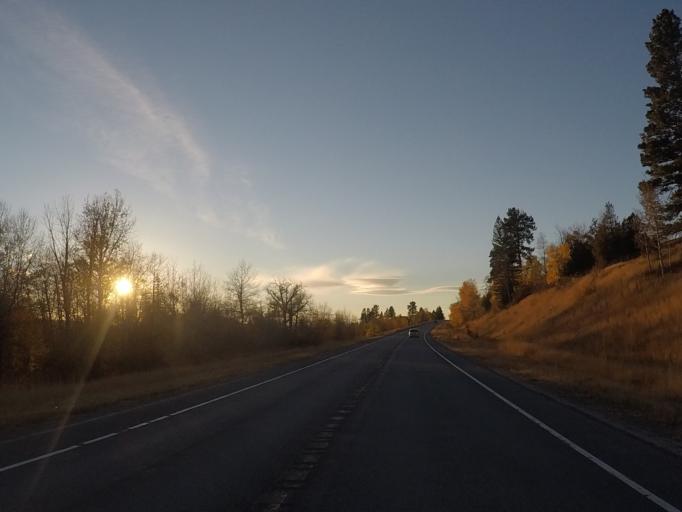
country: US
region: Montana
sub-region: Lewis and Clark County
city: Lincoln
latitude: 47.0176
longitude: -113.0849
